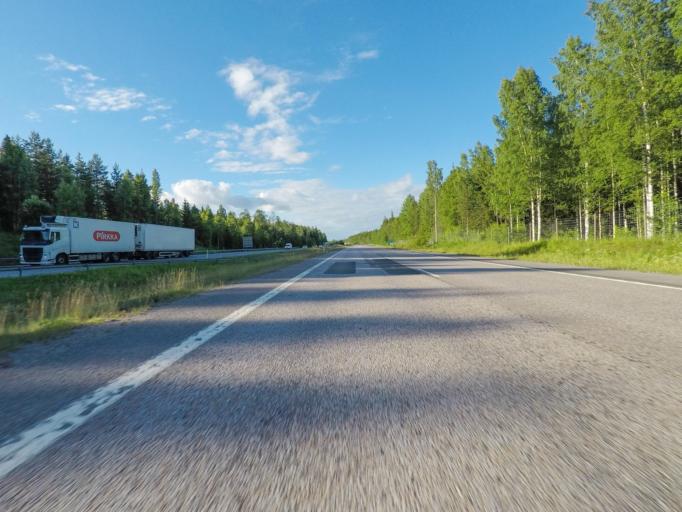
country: FI
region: Uusimaa
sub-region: Porvoo
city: Pukkila
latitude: 60.7789
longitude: 25.4795
